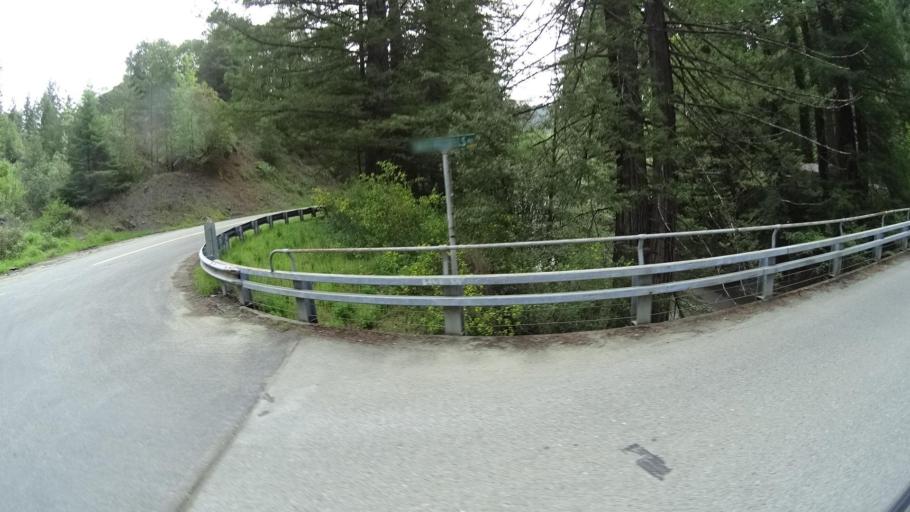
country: US
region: California
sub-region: Humboldt County
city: Redway
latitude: 40.2359
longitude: -123.8349
